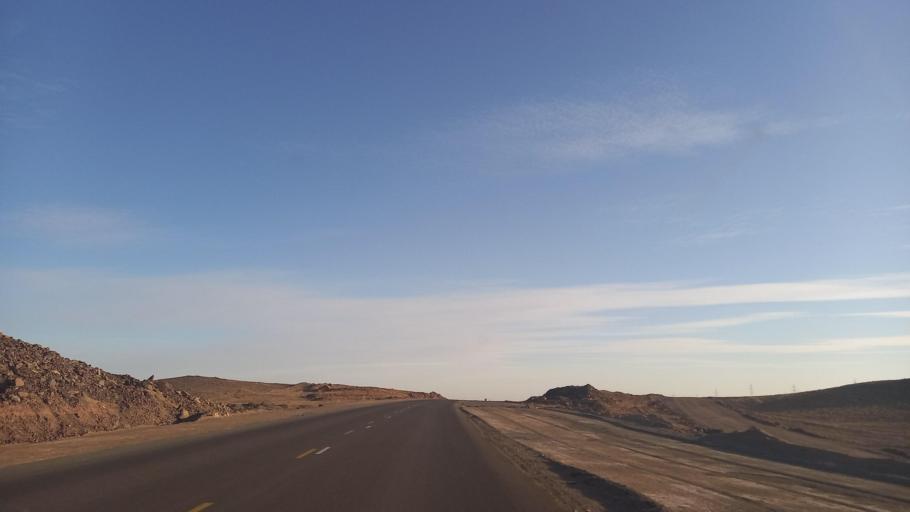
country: KZ
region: Zhambyl
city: Mynaral
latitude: 45.3034
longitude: 73.7613
